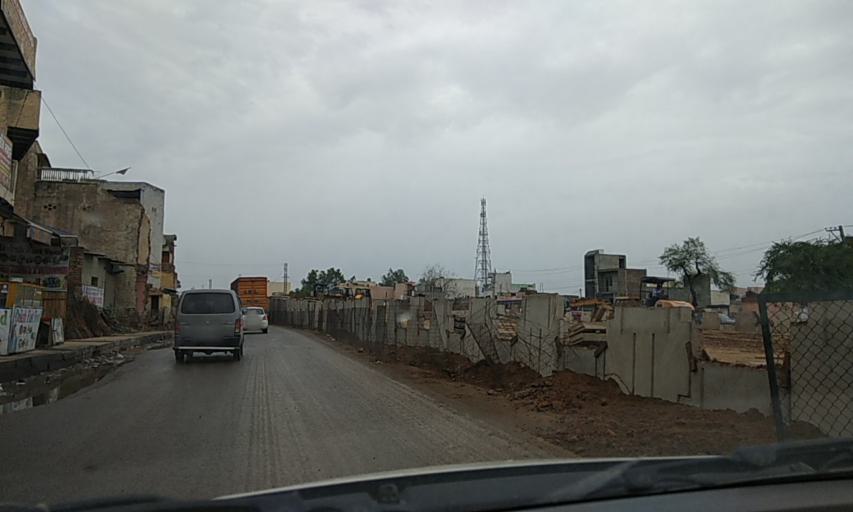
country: IN
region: Haryana
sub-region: Palwal
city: Palwal
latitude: 28.0586
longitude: 77.3468
